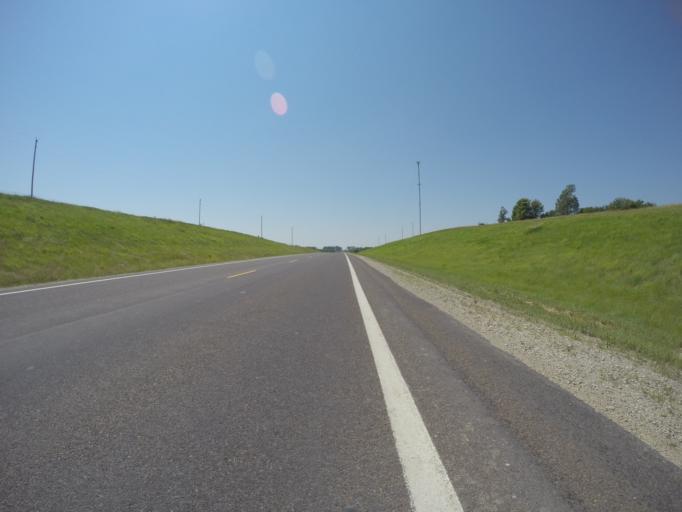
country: US
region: Kansas
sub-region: Doniphan County
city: Highland
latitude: 39.8495
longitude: -95.2652
